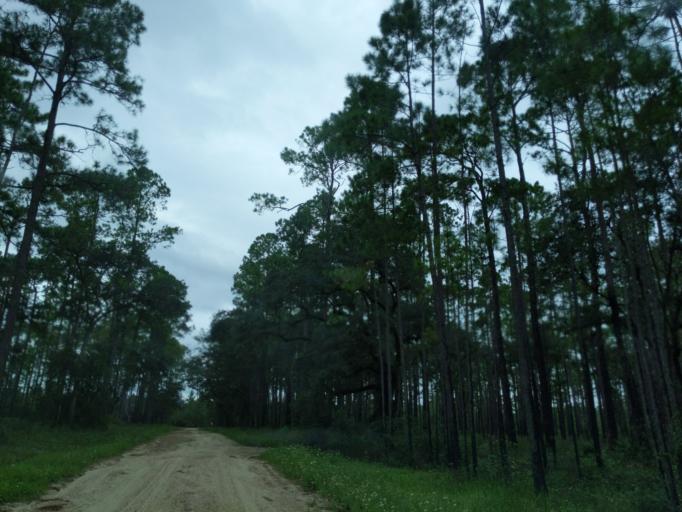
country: US
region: Florida
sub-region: Gadsden County
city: Midway
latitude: 30.3982
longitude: -84.4642
